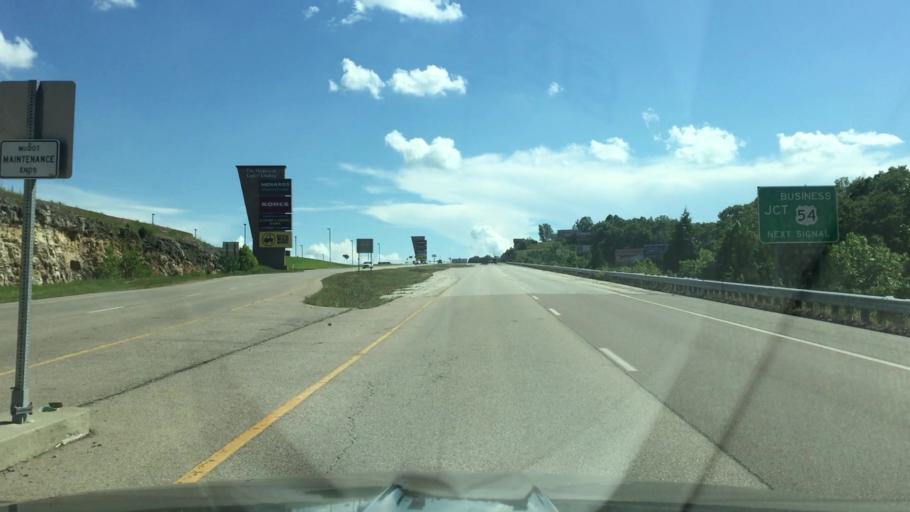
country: US
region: Missouri
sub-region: Miller County
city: Lake Ozark
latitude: 38.1819
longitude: -92.6114
